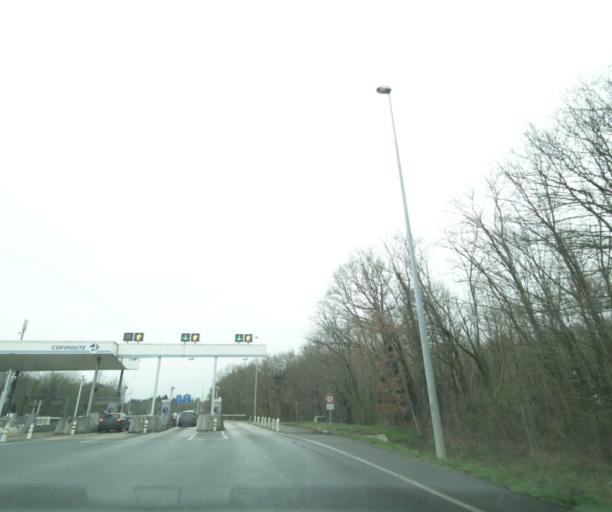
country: FR
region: Centre
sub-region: Departement du Loiret
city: Olivet
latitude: 47.8409
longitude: 1.8699
